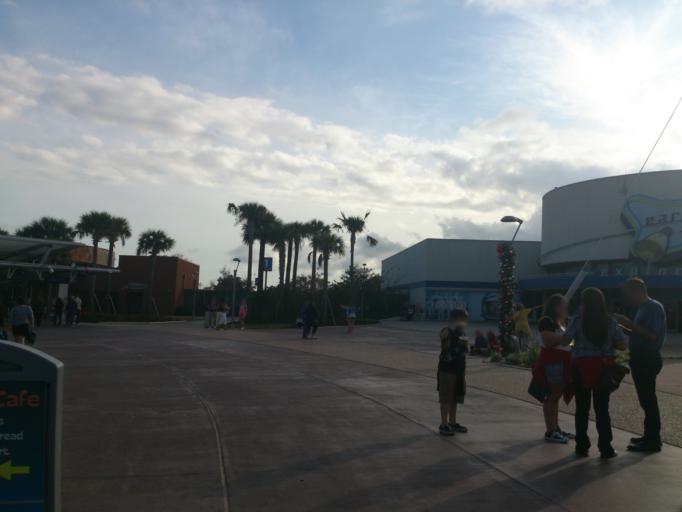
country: US
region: Florida
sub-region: Brevard County
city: Merritt Island
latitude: 28.5232
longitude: -80.6827
